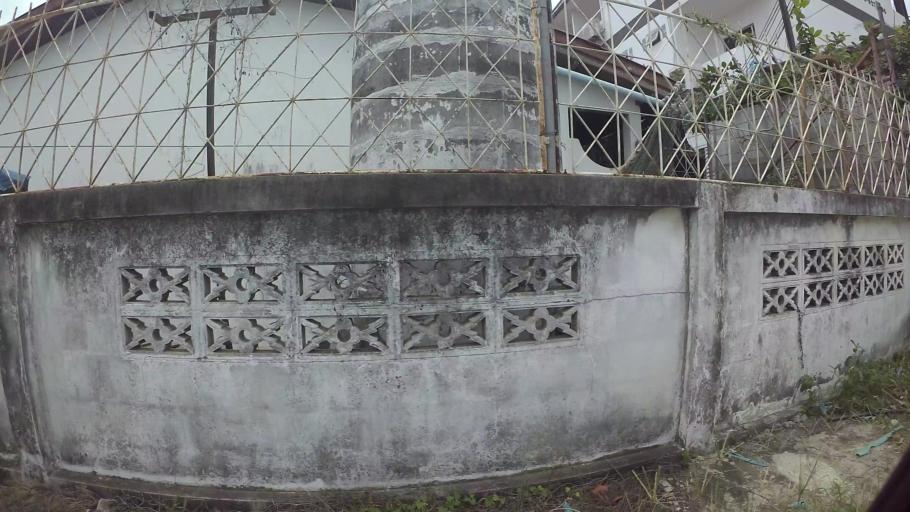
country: TH
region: Chon Buri
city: Sattahip
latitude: 12.7578
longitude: 100.8980
